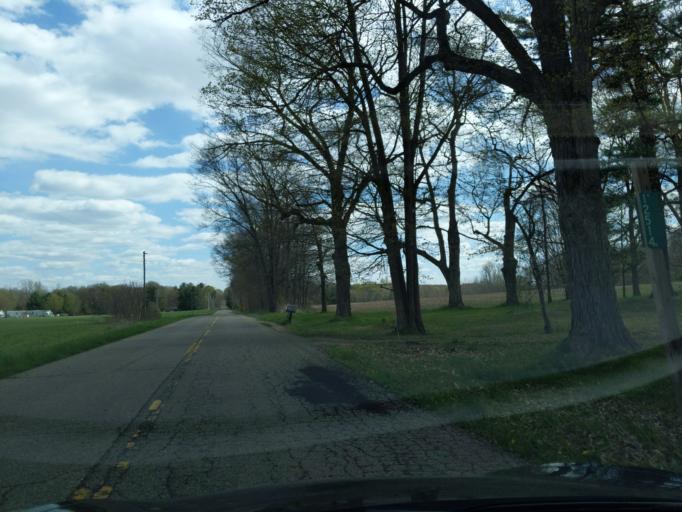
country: US
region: Michigan
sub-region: Ingham County
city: Leslie
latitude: 42.4114
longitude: -84.5268
